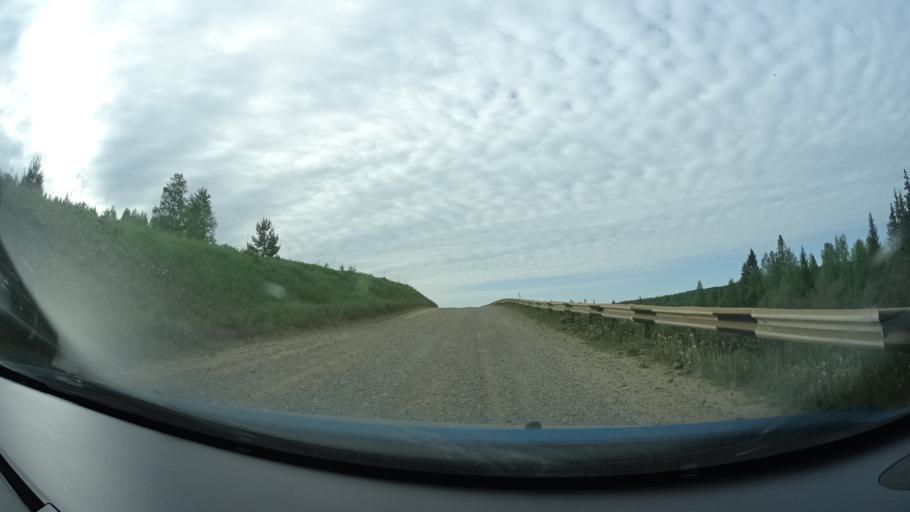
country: RU
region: Perm
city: Kuyeda
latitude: 56.6485
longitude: 55.6998
